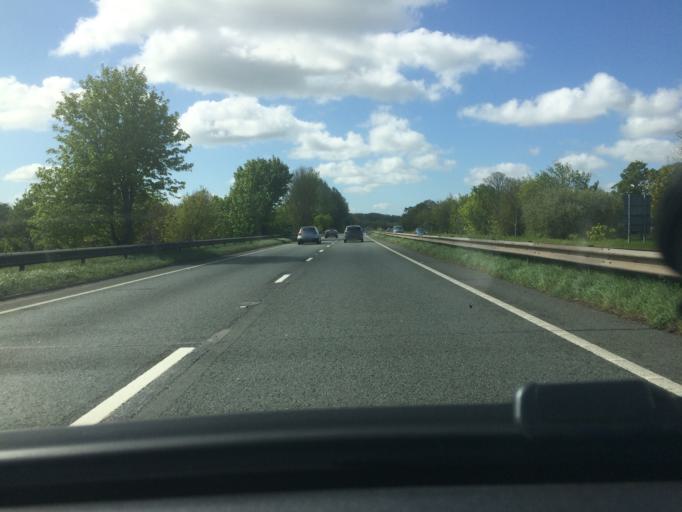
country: GB
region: Wales
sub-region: Wrexham
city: Rossett
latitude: 53.1126
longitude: -2.9531
